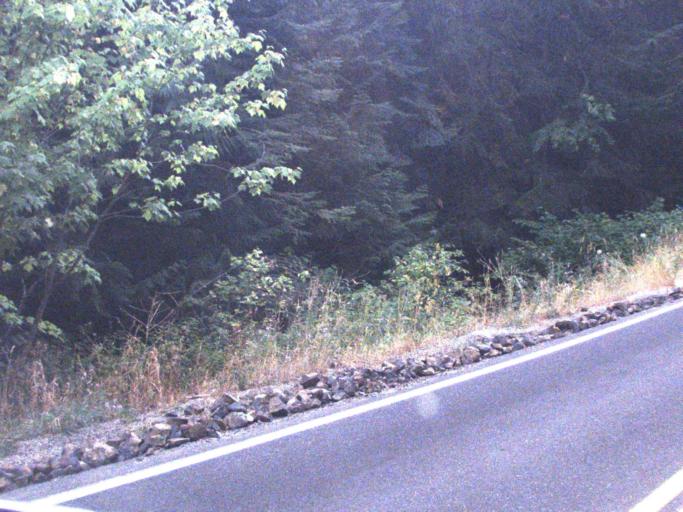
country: US
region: Washington
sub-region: Spokane County
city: Otis Orchards-East Farms
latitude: 47.8786
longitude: -117.1459
